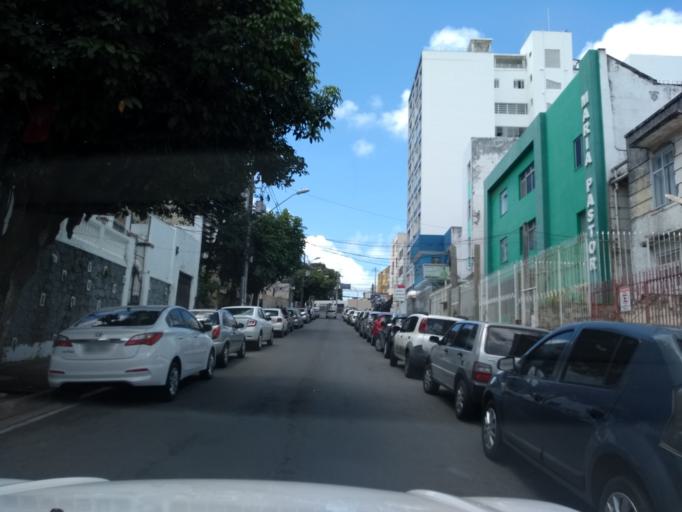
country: BR
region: Bahia
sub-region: Salvador
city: Salvador
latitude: -12.9791
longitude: -38.5090
